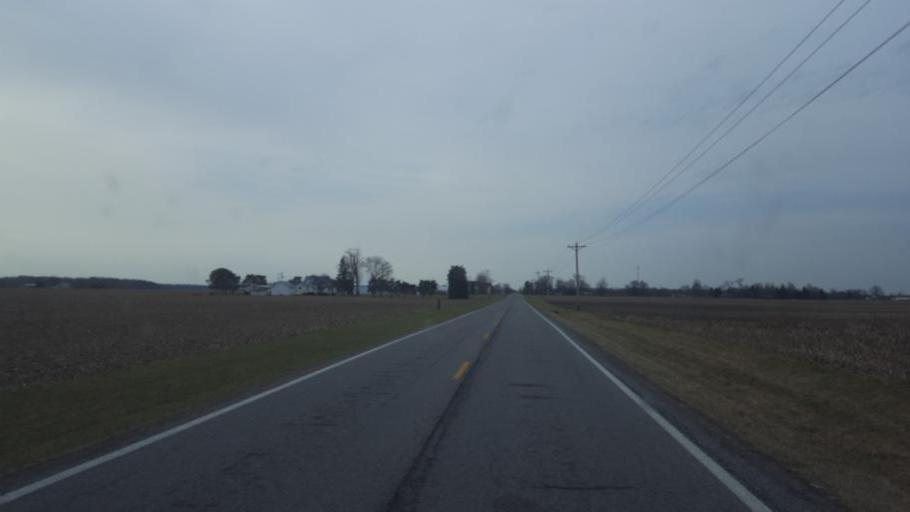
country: US
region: Ohio
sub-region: Morrow County
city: Cardington
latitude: 40.5952
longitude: -82.9624
